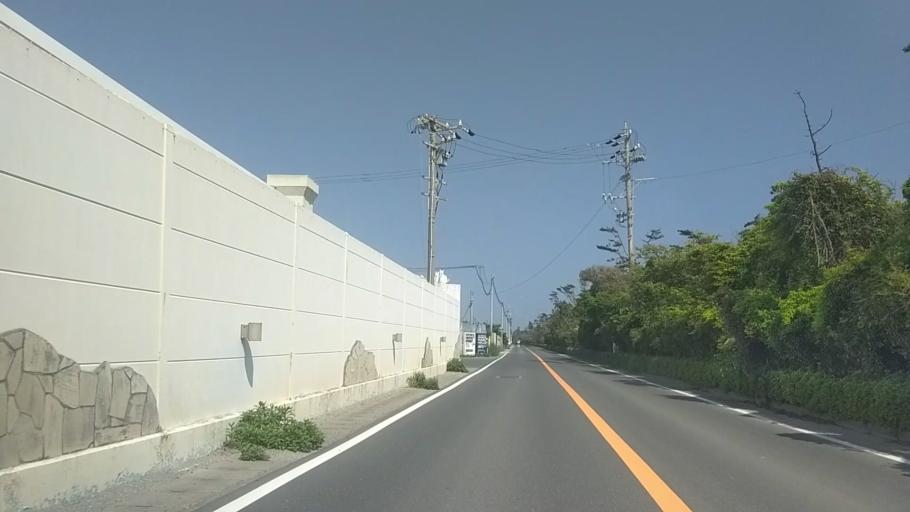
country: JP
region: Shizuoka
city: Hamamatsu
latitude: 34.6697
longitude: 137.6954
